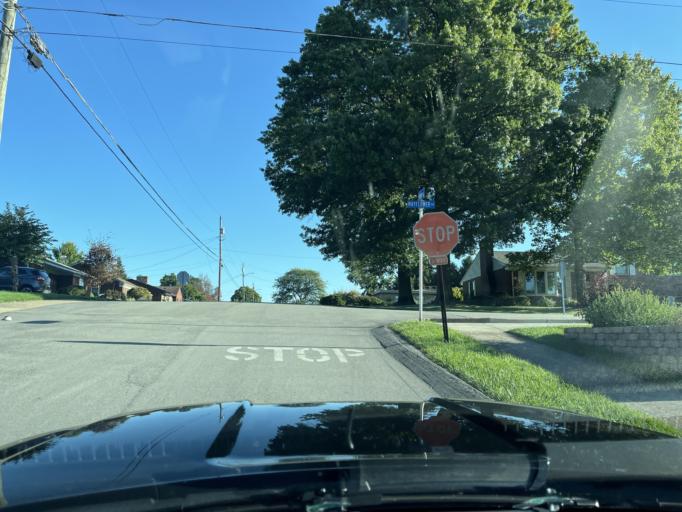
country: US
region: Pennsylvania
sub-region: Fayette County
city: Leith-Hatfield
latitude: 39.8783
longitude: -79.7360
